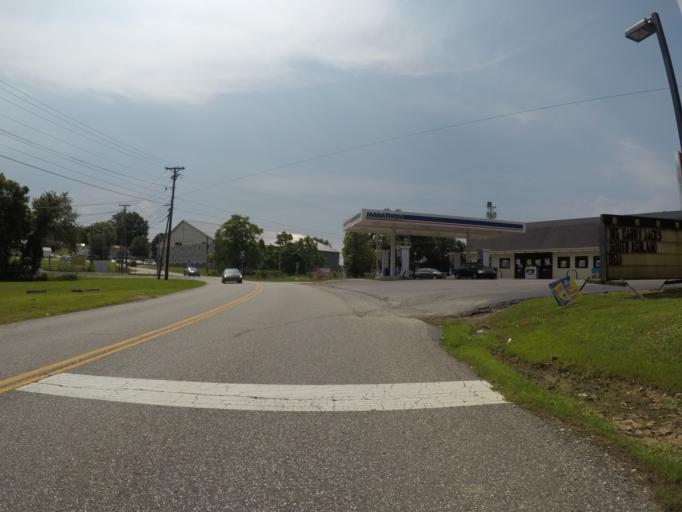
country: US
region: Kentucky
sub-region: Boyd County
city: Ironville
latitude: 38.4407
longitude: -82.7078
